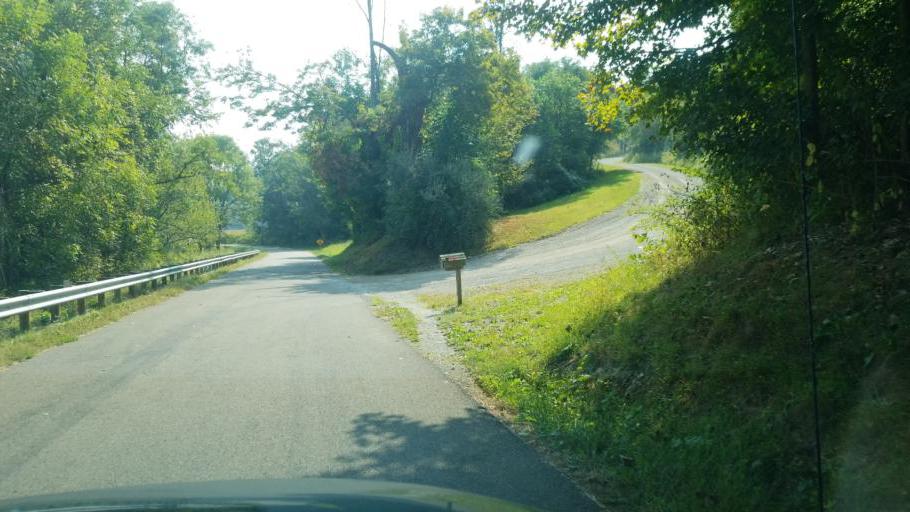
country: US
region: Ohio
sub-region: Licking County
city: Utica
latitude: 40.1931
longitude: -82.4481
